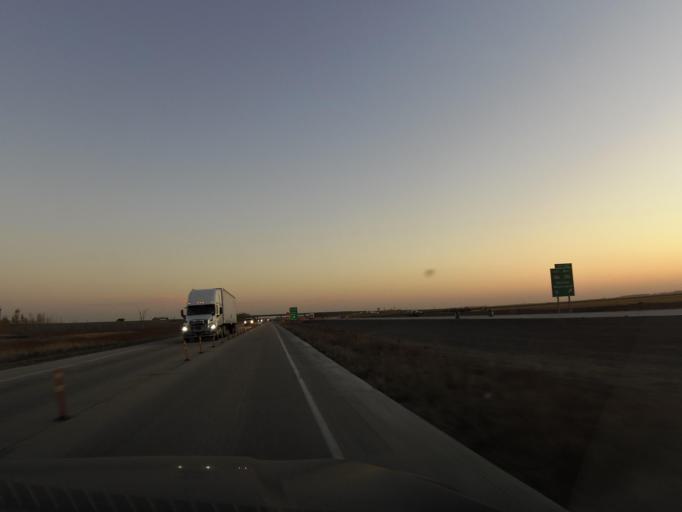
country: US
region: North Dakota
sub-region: Traill County
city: Hillsboro
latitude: 47.3588
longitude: -97.0503
